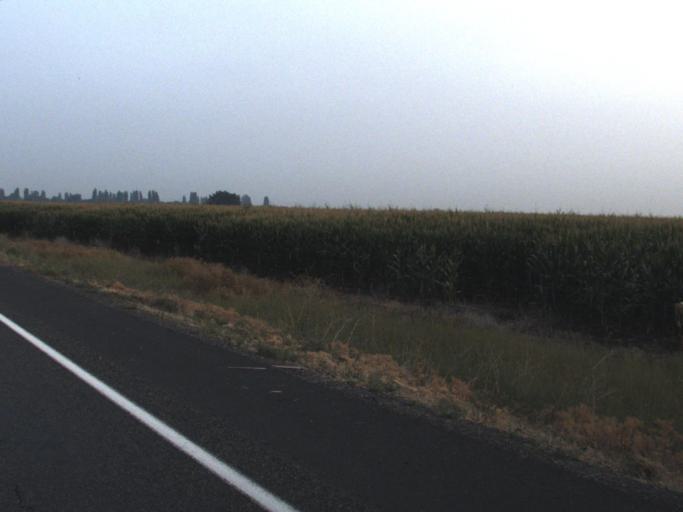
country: US
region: Washington
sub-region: Yakima County
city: Toppenish
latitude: 46.3220
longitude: -120.3206
